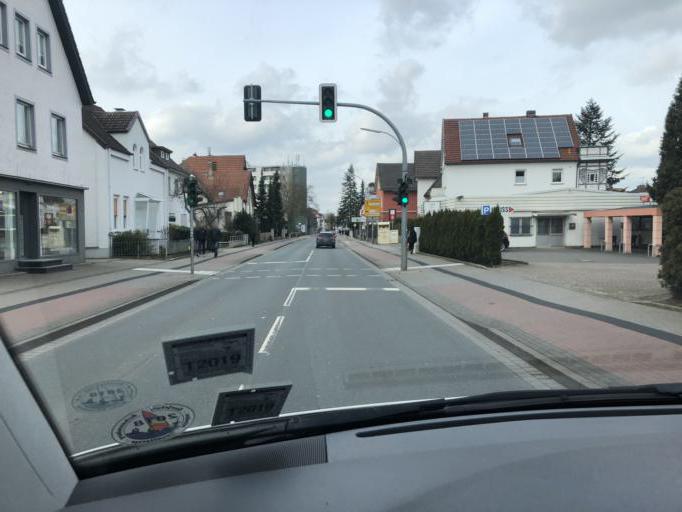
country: DE
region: North Rhine-Westphalia
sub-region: Regierungsbezirk Detmold
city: Herford
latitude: 52.1087
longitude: 8.6749
